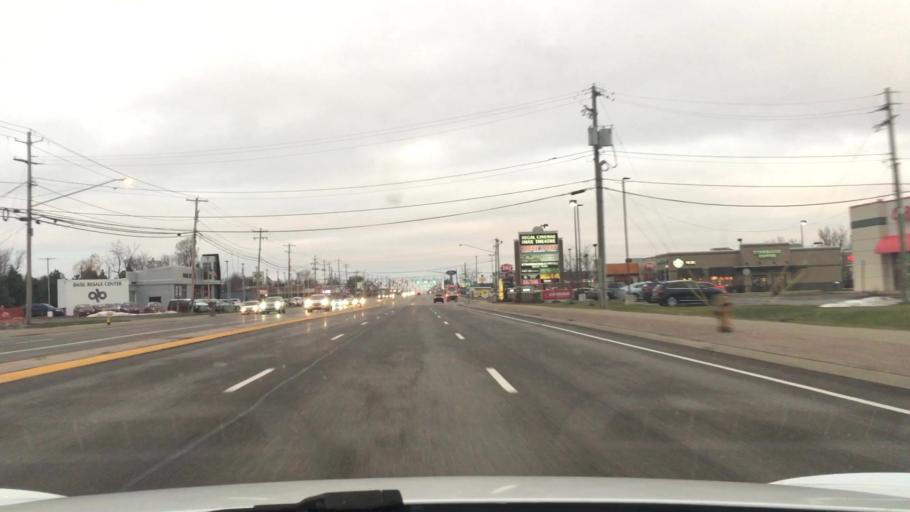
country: US
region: New York
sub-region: Erie County
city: Harris Hill
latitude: 42.9533
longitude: -78.6969
